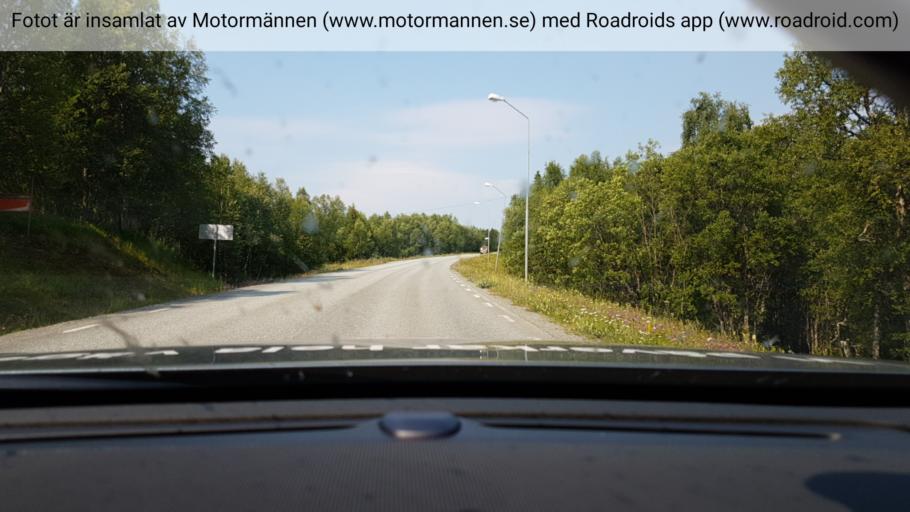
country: NO
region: Nordland
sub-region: Rana
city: Mo i Rana
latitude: 65.7180
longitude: 15.2079
